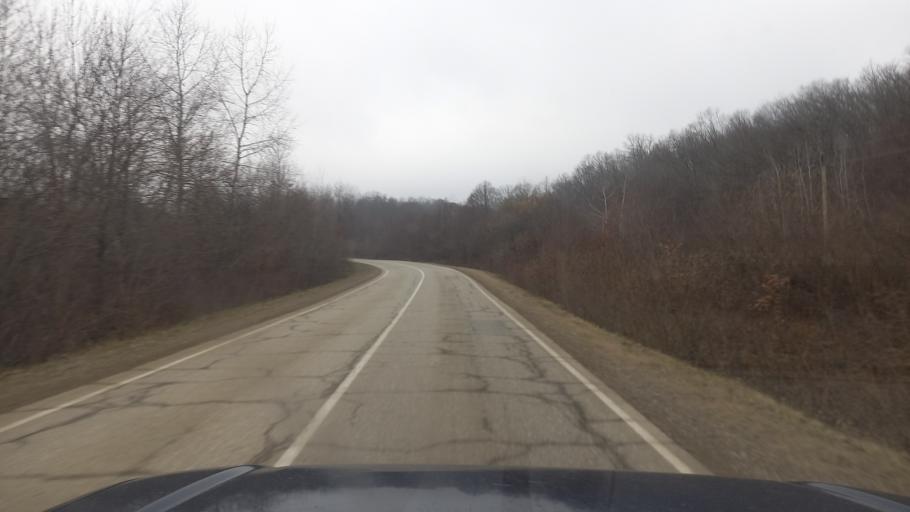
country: RU
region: Krasnodarskiy
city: Neftegorsk
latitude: 44.2847
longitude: 39.8023
